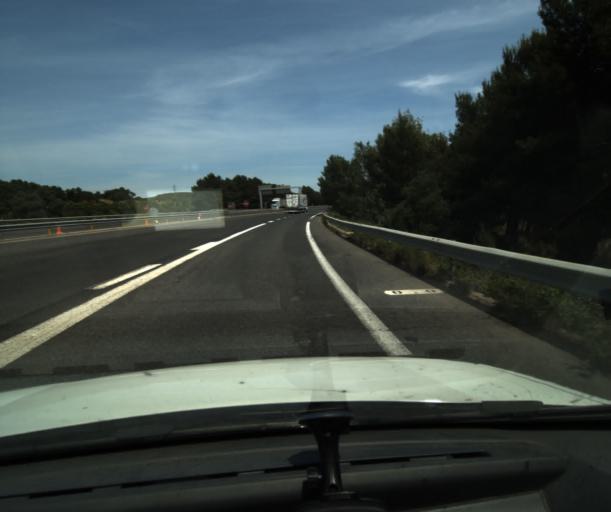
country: FR
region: Languedoc-Roussillon
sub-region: Departement des Pyrenees-Orientales
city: el Volo
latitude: 42.5295
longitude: 2.8232
